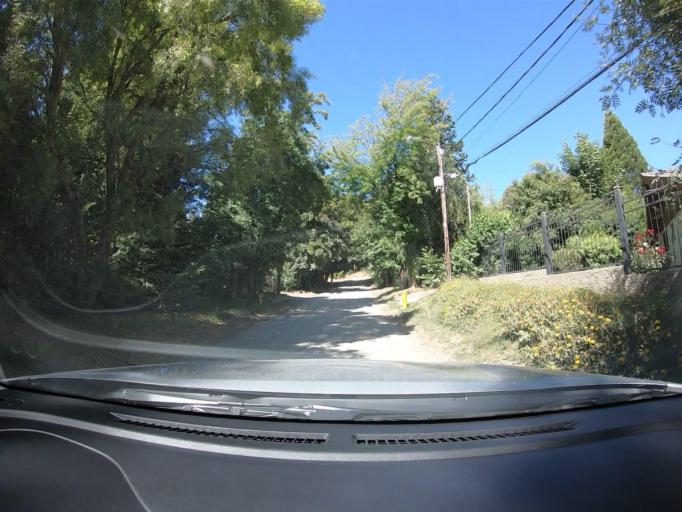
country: AR
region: Rio Negro
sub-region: Departamento de Bariloche
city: San Carlos de Bariloche
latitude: -41.1232
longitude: -71.3926
